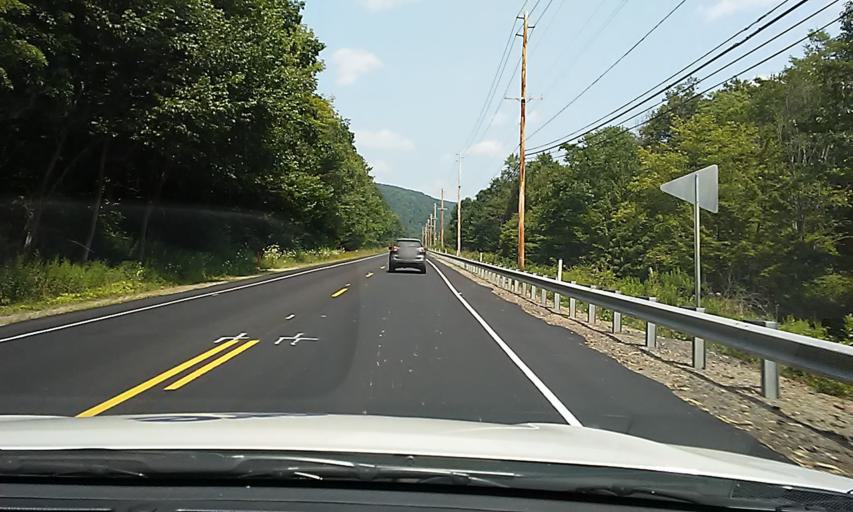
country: US
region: Pennsylvania
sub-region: Cameron County
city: Emporium
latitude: 41.4735
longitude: -78.3299
